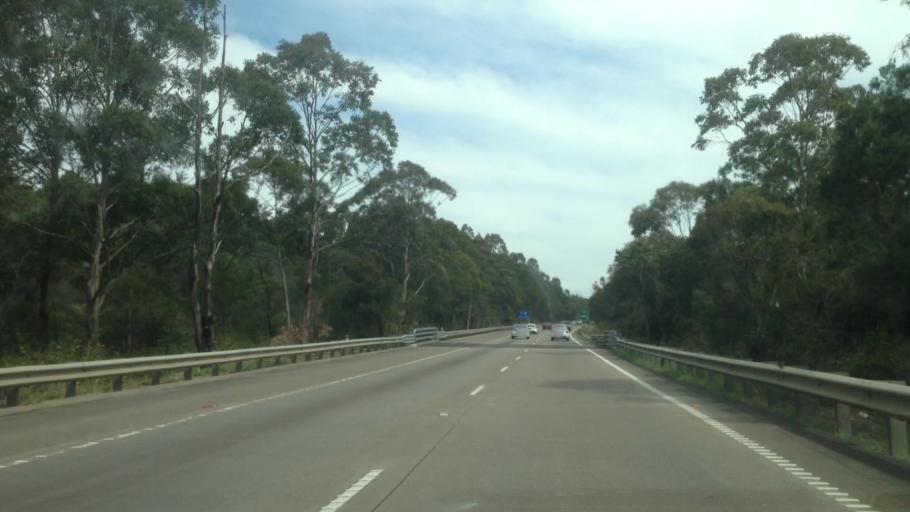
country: AU
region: New South Wales
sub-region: Lake Macquarie Shire
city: Fennell Bay
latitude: -32.9721
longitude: 151.5334
